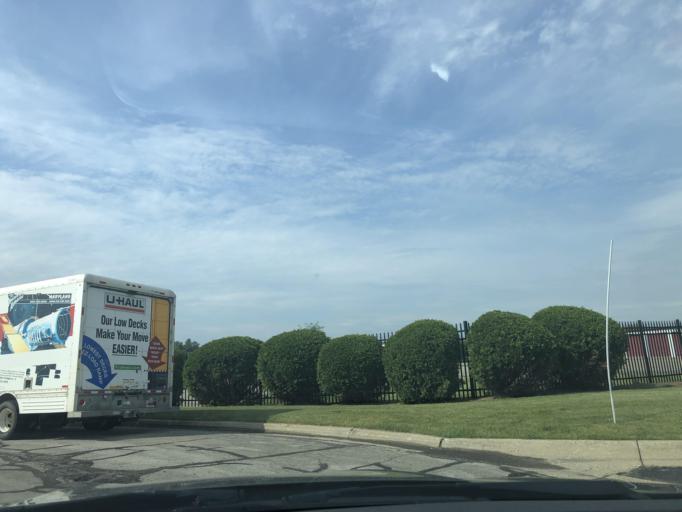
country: US
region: Michigan
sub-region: Ingham County
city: East Lansing
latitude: 42.7759
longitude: -84.4806
